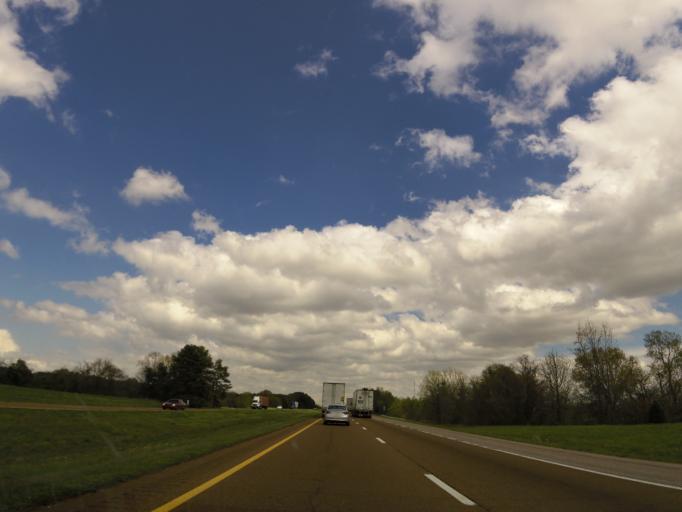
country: US
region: Tennessee
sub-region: Tipton County
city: Mason
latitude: 35.3593
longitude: -89.4956
